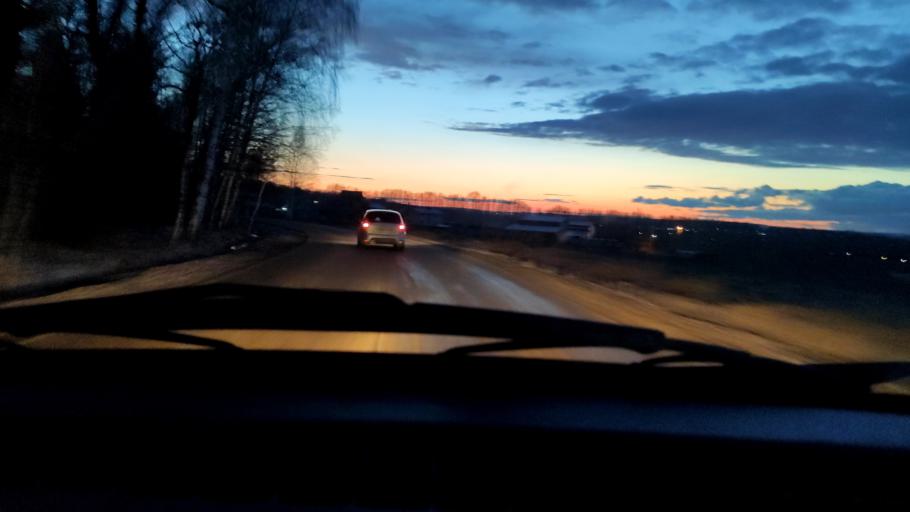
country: RU
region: Bashkortostan
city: Avdon
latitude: 54.4777
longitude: 55.8694
